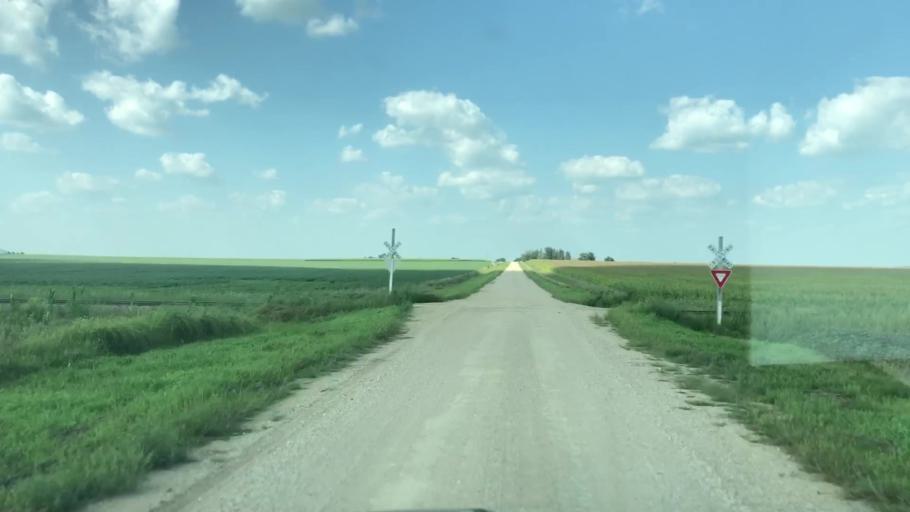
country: US
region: Iowa
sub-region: O'Brien County
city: Sheldon
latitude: 43.1781
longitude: -95.7824
